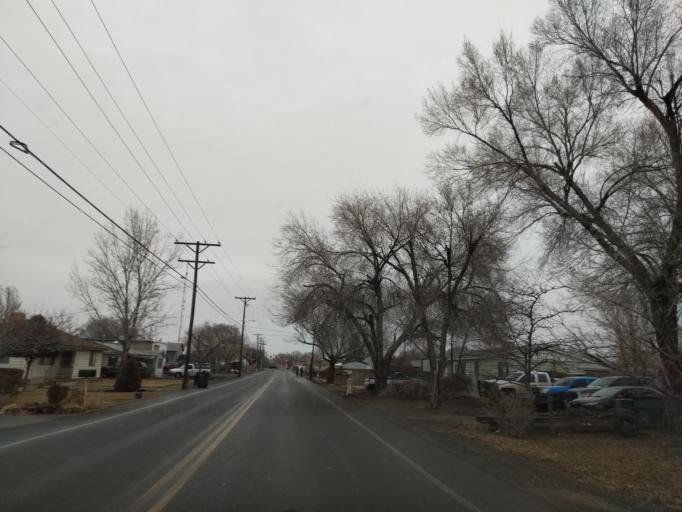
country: US
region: Colorado
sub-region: Mesa County
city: Grand Junction
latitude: 39.0747
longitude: -108.5244
